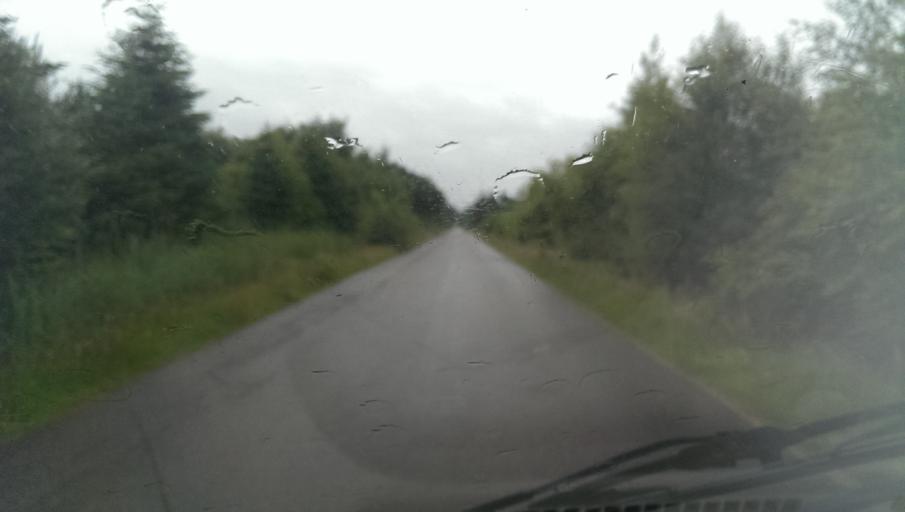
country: DK
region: Central Jutland
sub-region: Holstebro Kommune
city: Ulfborg
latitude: 56.2654
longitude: 8.1514
